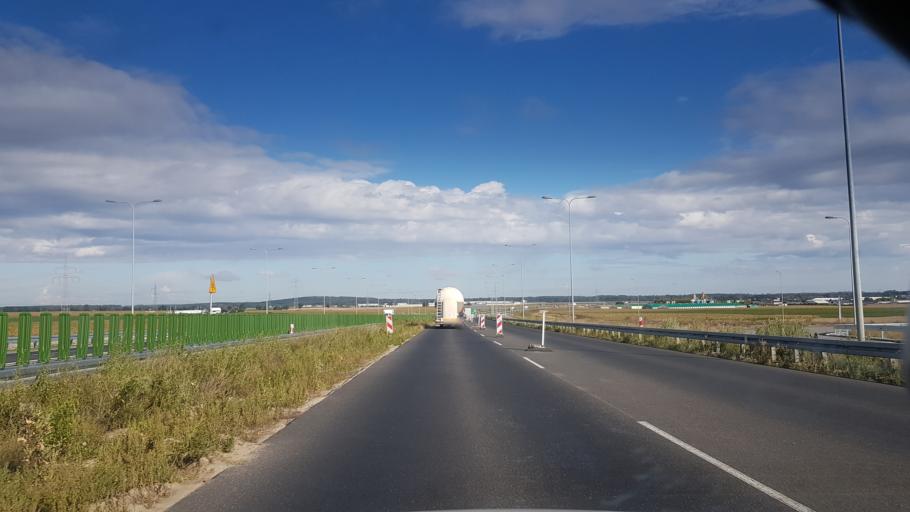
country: PL
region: Greater Poland Voivodeship
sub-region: Powiat poznanski
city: Steszew
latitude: 52.2689
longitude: 16.6679
